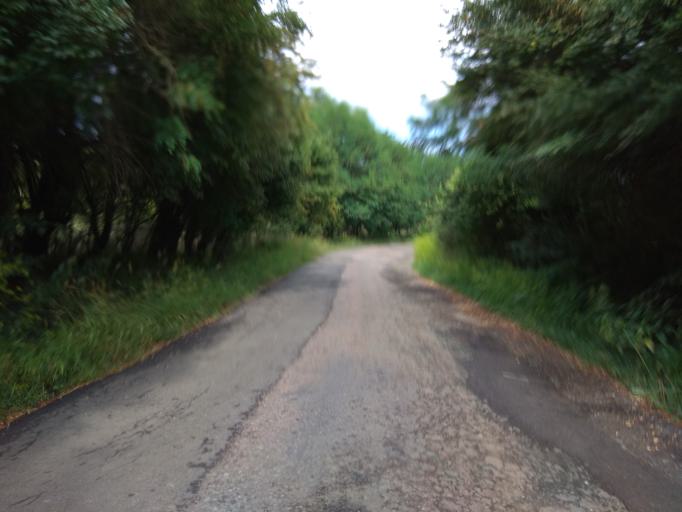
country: HU
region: Heves
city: Belapatfalva
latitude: 48.0266
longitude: 20.2787
